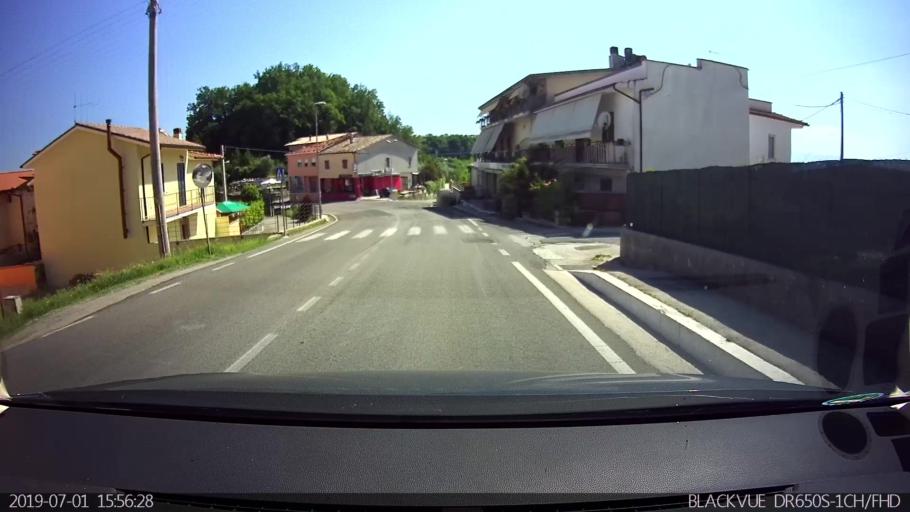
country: IT
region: Latium
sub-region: Provincia di Frosinone
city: Veroli
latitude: 41.6823
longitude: 13.4173
